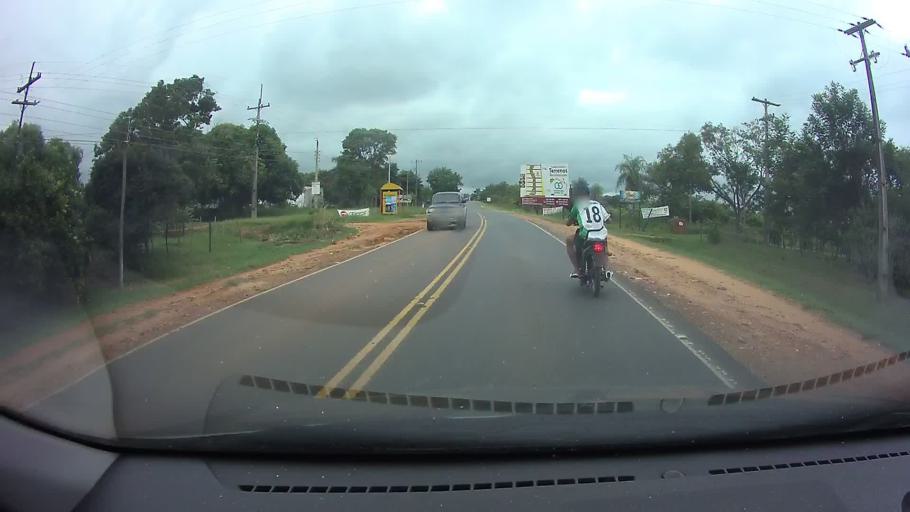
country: PY
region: Central
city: Guarambare
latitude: -25.5125
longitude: -57.4889
